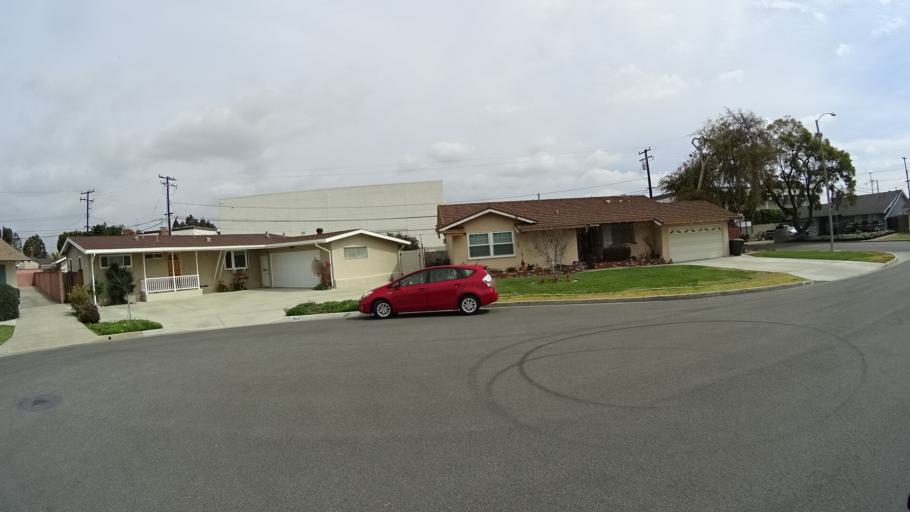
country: US
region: California
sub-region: Orange County
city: Stanton
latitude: 33.8189
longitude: -117.9862
